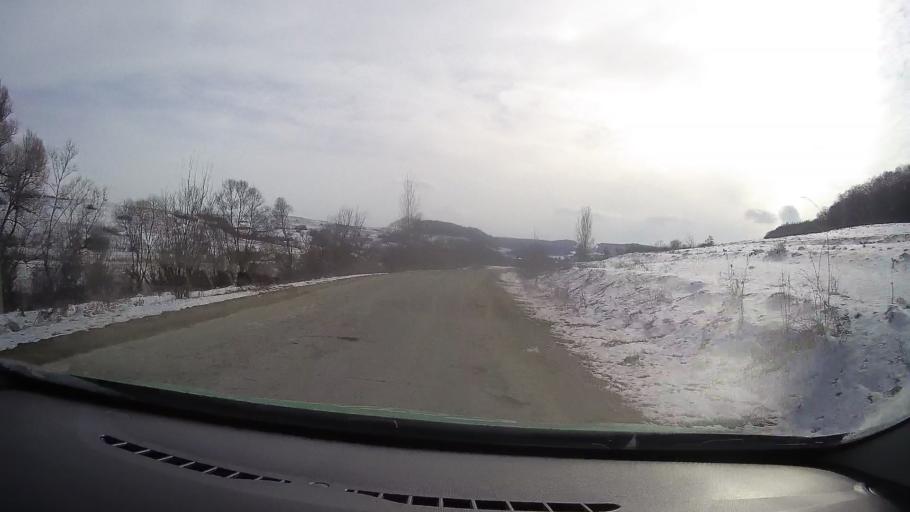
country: RO
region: Sibiu
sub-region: Comuna Bradeni
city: Bradeni
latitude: 46.0914
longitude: 24.8339
